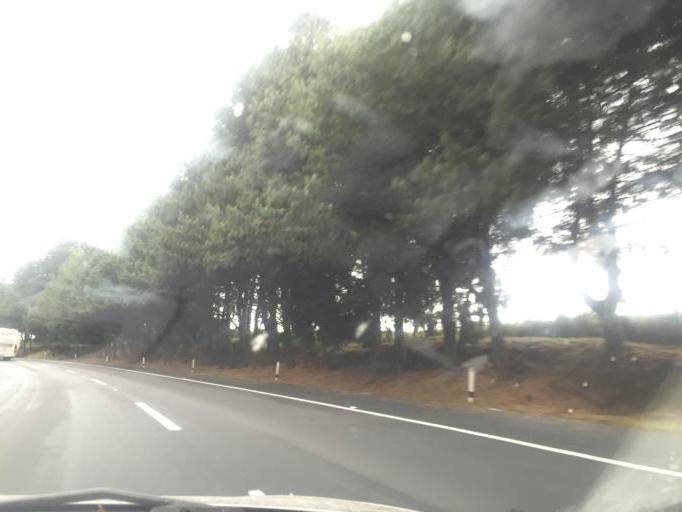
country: MX
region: Mexico City
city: Xochimilco
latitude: 19.1642
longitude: -99.1542
